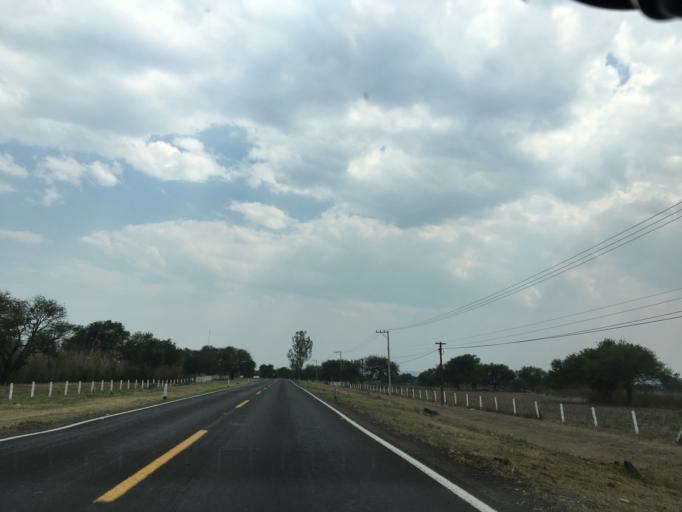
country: MX
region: Michoacan
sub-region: Cuitzeo
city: Cuamio
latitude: 20.0036
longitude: -101.1556
